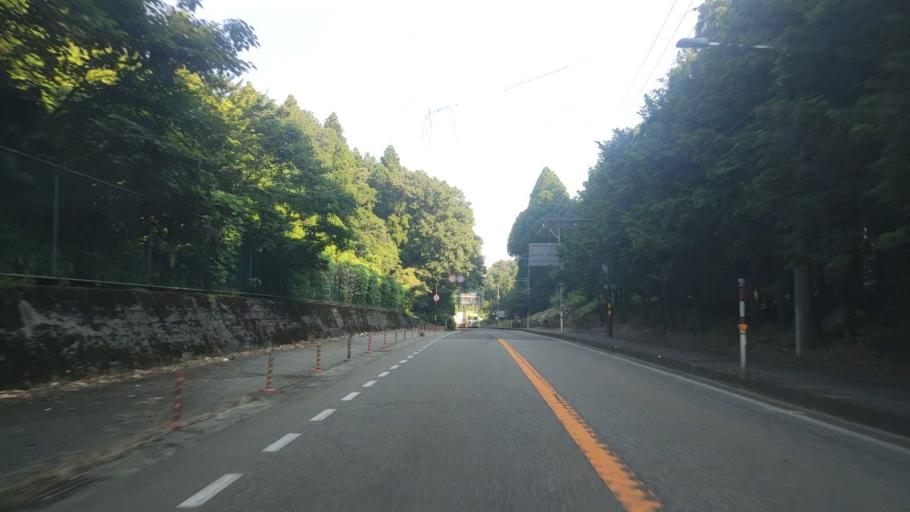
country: JP
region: Fukui
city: Maruoka
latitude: 36.2388
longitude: 136.2858
